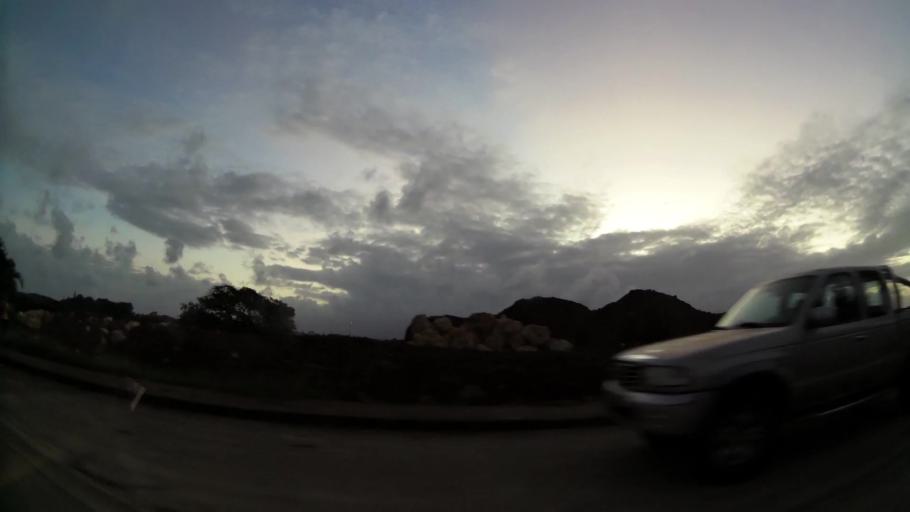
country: GP
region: Guadeloupe
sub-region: Guadeloupe
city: Les Abymes
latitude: 16.2652
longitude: -61.5156
